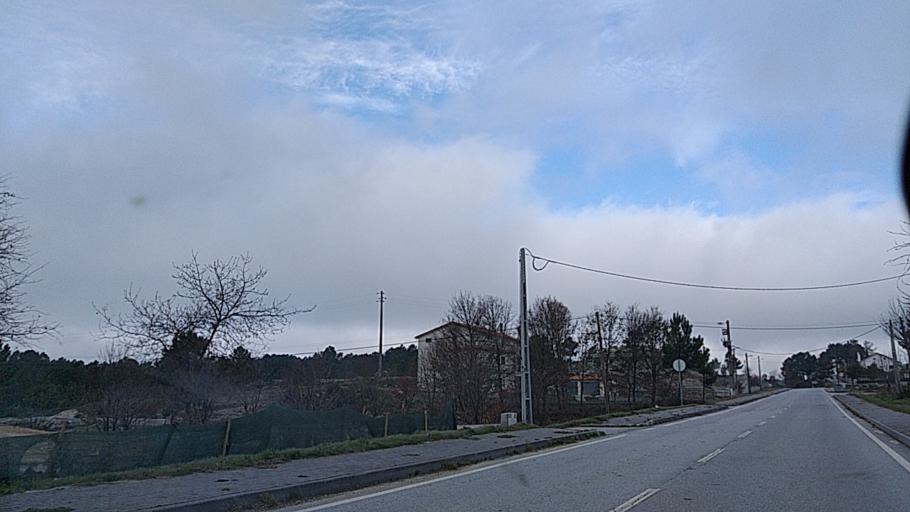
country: PT
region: Guarda
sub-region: Aguiar da Beira
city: Aguiar da Beira
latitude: 40.7417
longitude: -7.4966
